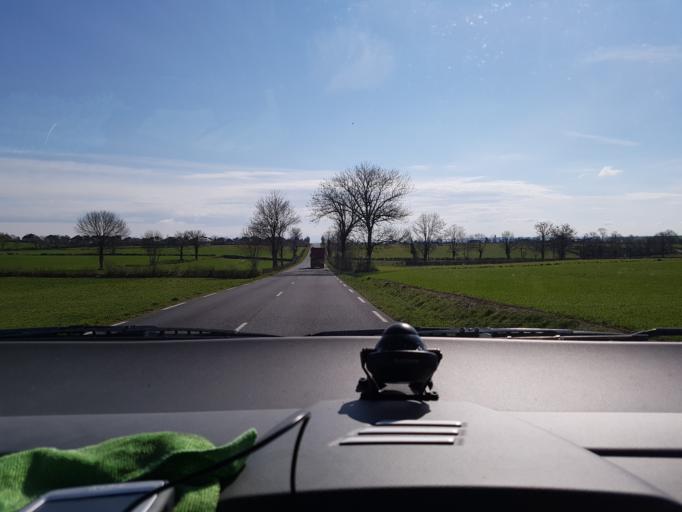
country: FR
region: Midi-Pyrenees
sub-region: Departement de l'Aveyron
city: Druelle
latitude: 44.3693
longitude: 2.5055
